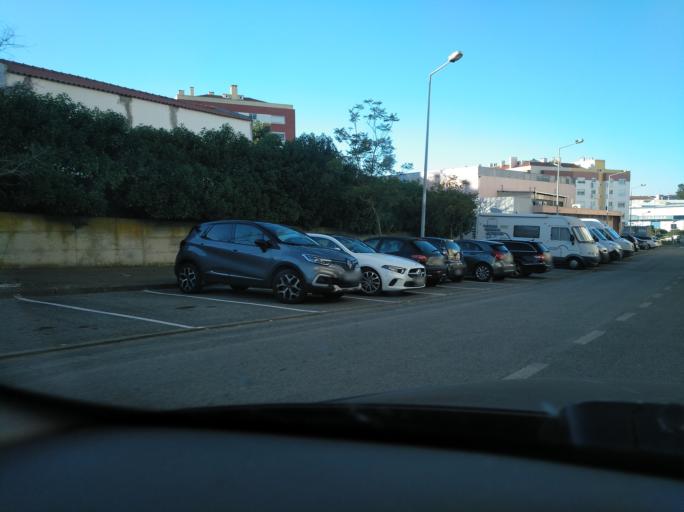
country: PT
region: Lisbon
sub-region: Loures
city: Sacavem
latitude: 38.7932
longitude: -9.1185
